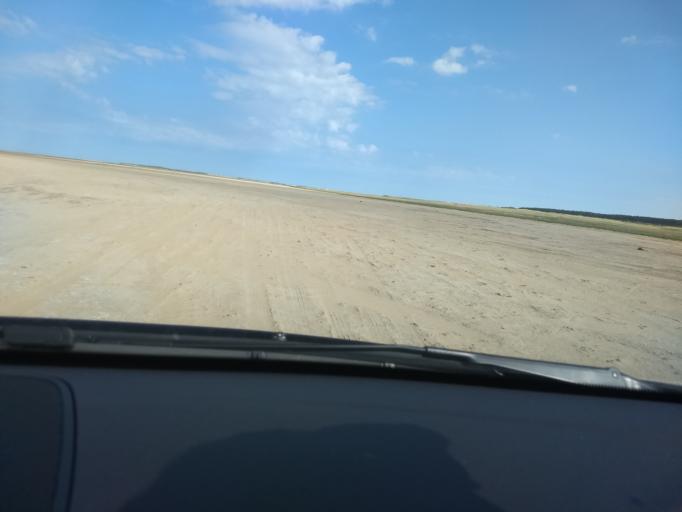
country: DE
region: Schleswig-Holstein
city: List
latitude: 55.0901
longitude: 8.5000
